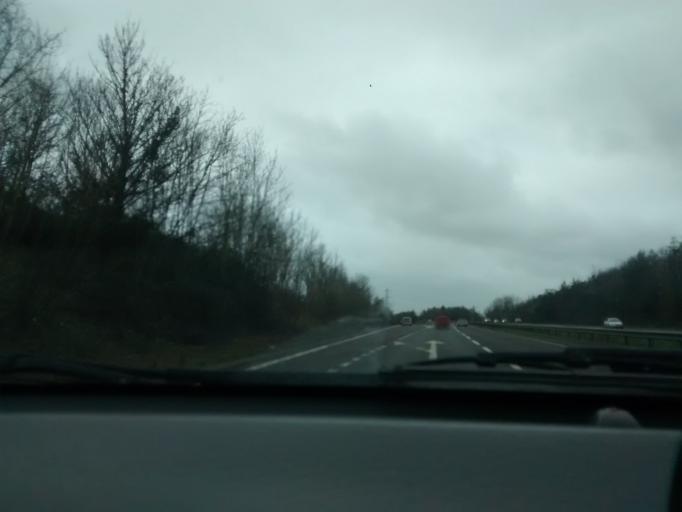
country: GB
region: England
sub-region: Suffolk
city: Needham Market
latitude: 52.1419
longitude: 1.0832
